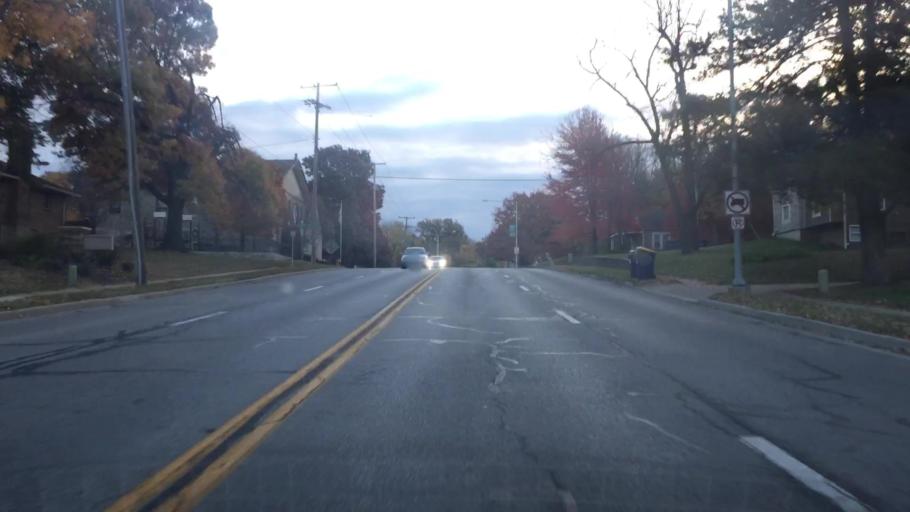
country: US
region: Kansas
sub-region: Johnson County
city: Merriam
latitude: 39.0229
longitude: -94.7119
